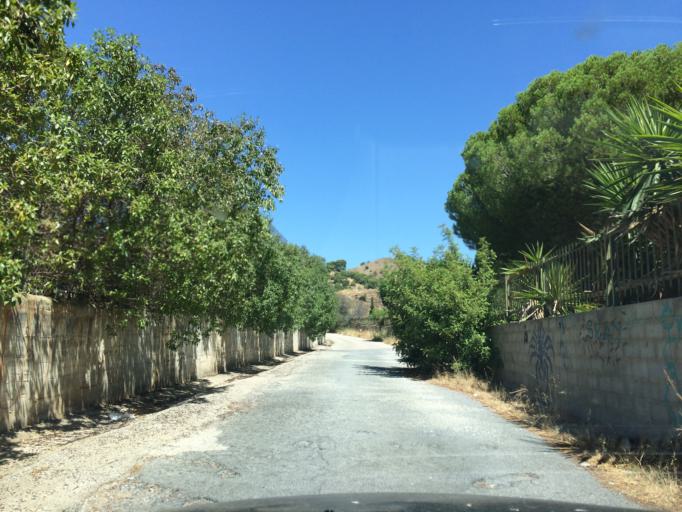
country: ES
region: Andalusia
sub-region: Provincia de Malaga
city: Malaga
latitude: 36.7355
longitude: -4.4652
